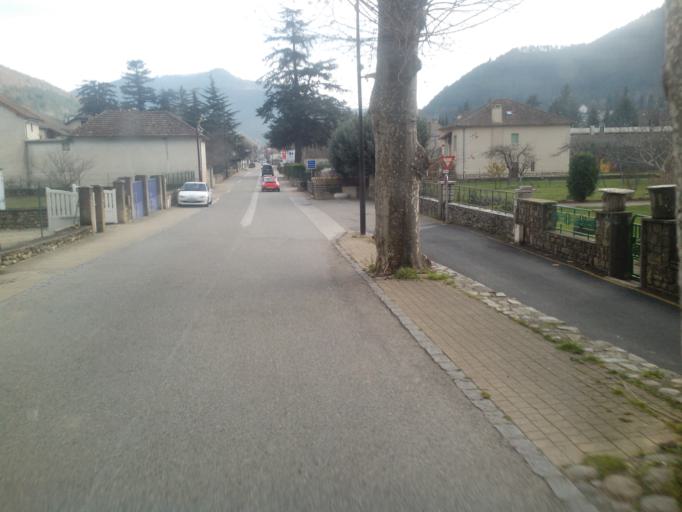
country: FR
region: Languedoc-Roussillon
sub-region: Departement de la Lozere
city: Florac
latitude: 44.3304
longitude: 3.5906
